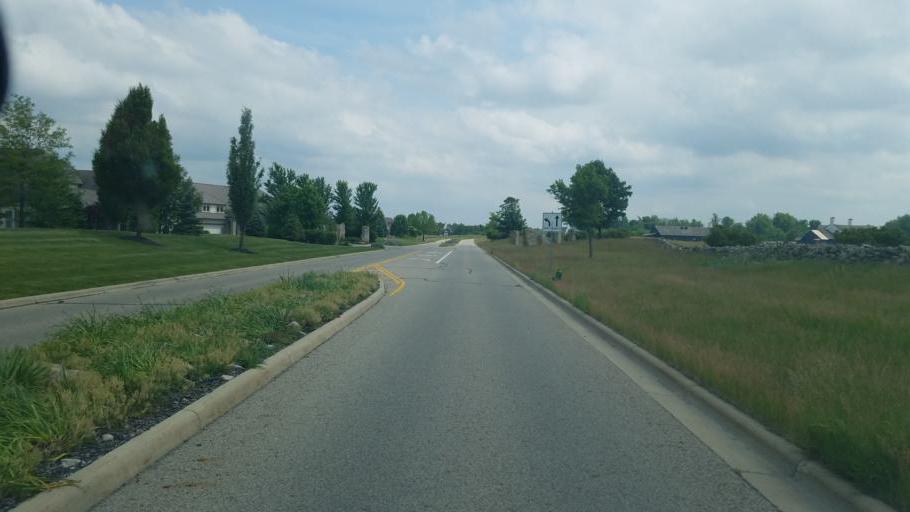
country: US
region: Ohio
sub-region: Franklin County
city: Hilliard
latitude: 40.0913
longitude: -83.1740
